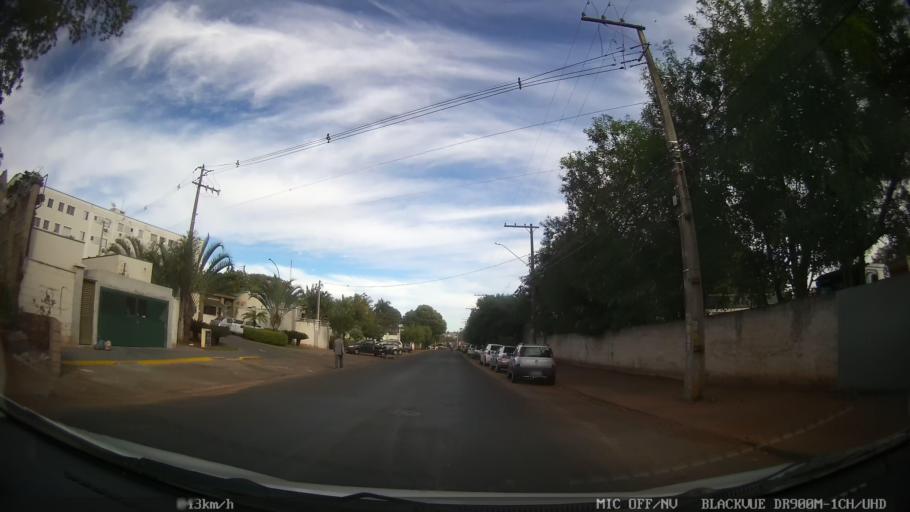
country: BR
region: Sao Paulo
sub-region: Catanduva
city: Catanduva
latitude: -21.1379
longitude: -48.9962
